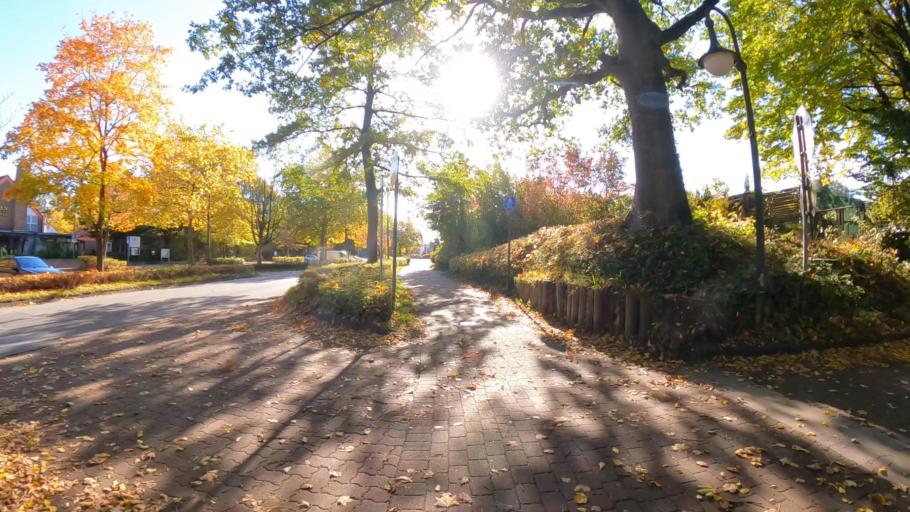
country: DE
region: Schleswig-Holstein
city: Ahrensburg
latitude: 53.6806
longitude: 10.2341
